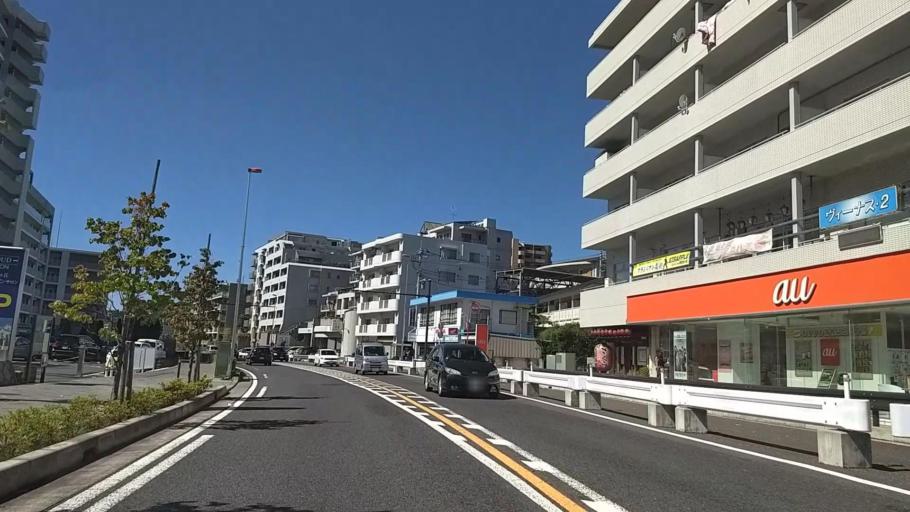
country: JP
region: Tokyo
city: Chofugaoka
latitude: 35.6054
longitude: 139.5048
